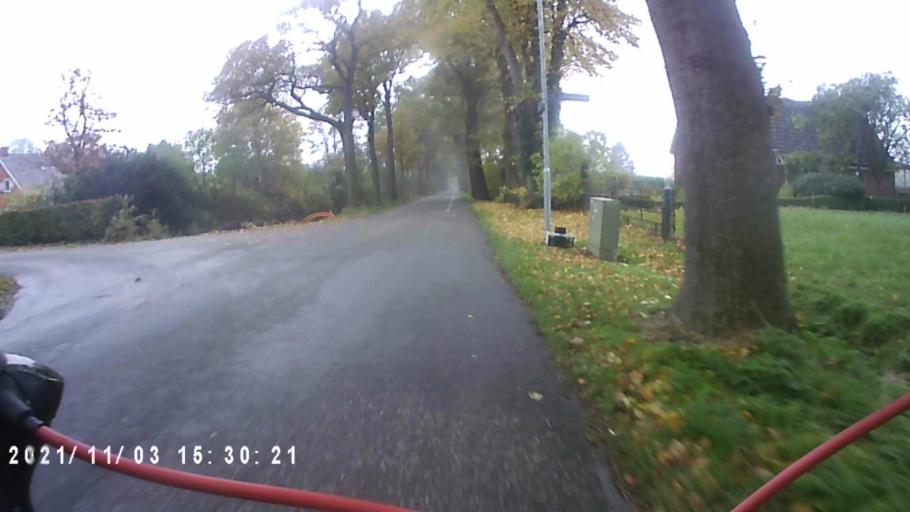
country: NL
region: Groningen
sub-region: Gemeente Leek
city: Leek
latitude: 53.1331
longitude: 6.3710
